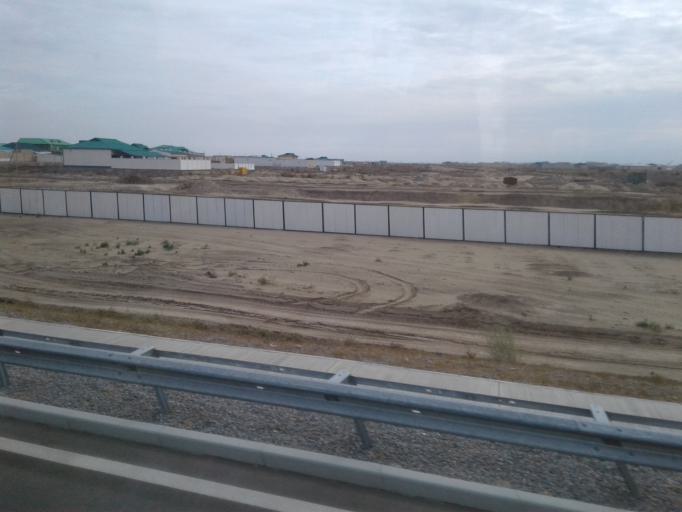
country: TM
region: Lebap
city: Turkmenabat
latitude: 38.9823
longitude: 63.5566
